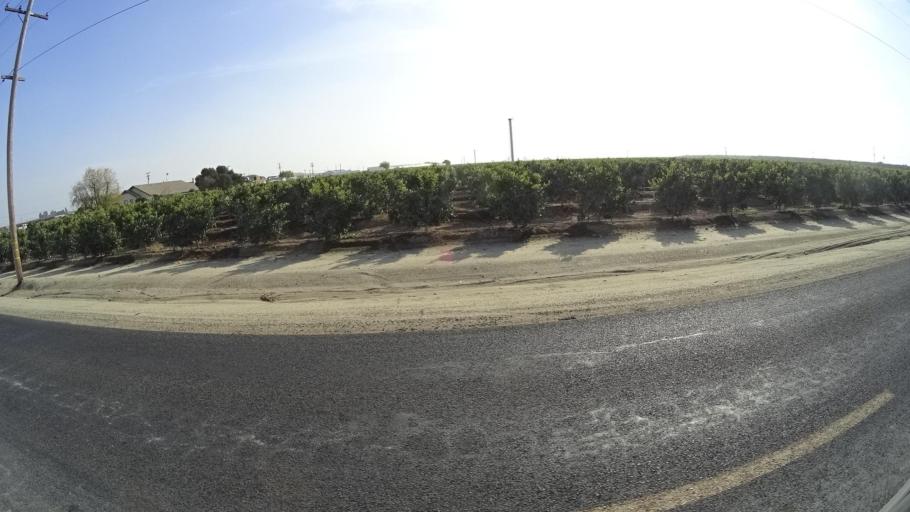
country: US
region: California
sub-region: Kern County
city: Delano
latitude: 35.7760
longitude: -119.2017
